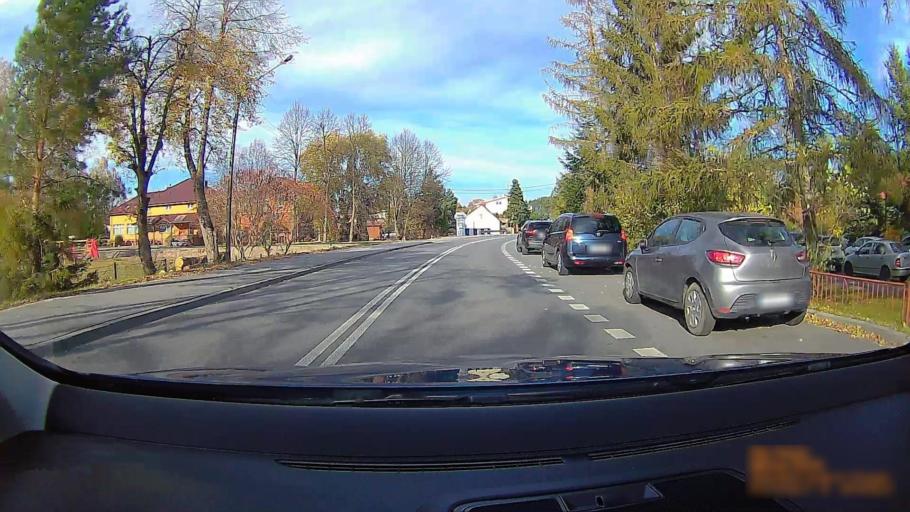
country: PL
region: Greater Poland Voivodeship
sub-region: Powiat ostrzeszowski
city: Doruchow
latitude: 51.3621
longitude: 18.0283
